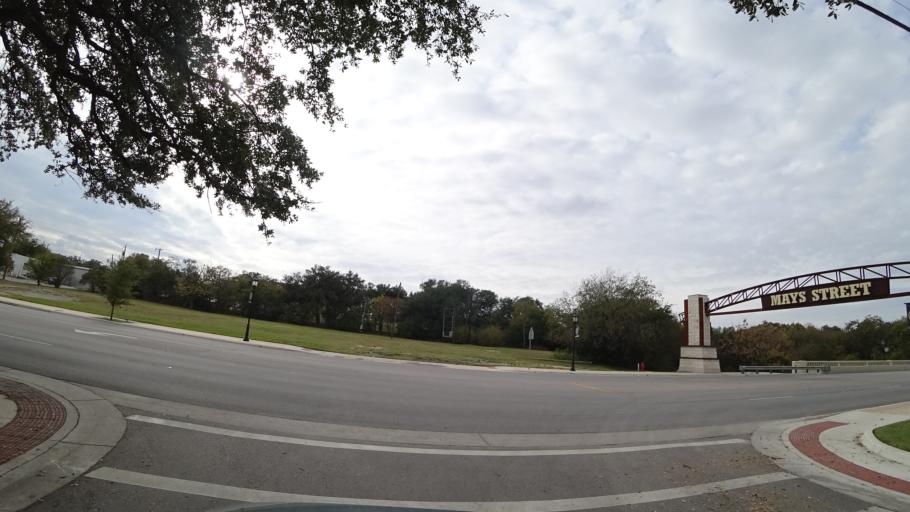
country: US
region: Texas
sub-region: Williamson County
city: Round Rock
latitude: 30.5125
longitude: -97.6803
